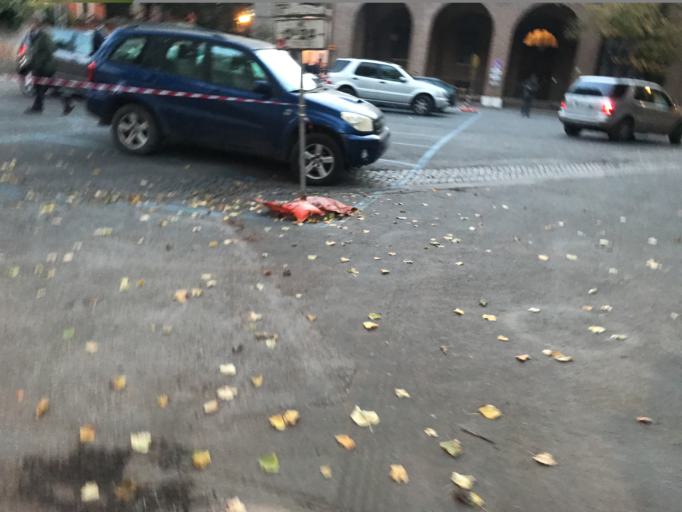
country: IT
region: Latium
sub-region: Citta metropolitana di Roma Capitale
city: Rome
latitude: 41.8846
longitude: 12.4803
